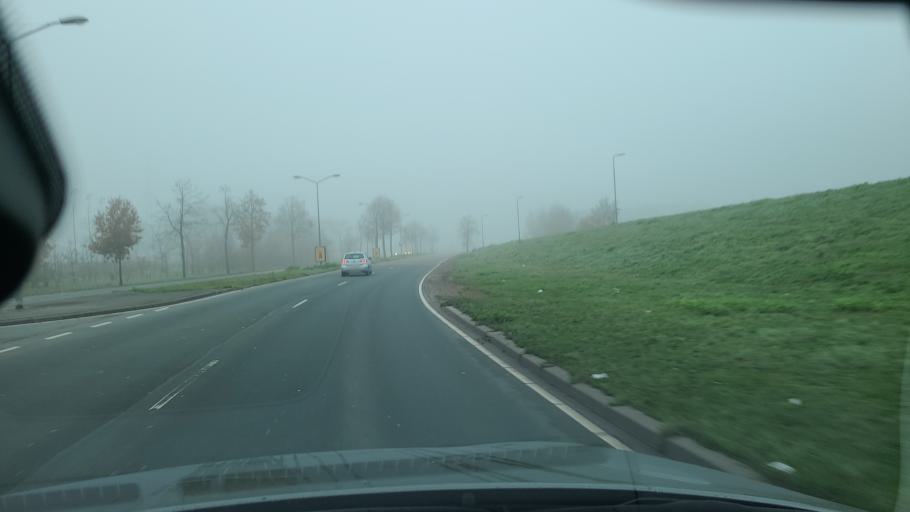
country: NL
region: North Brabant
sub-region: Gemeente 's-Hertogenbosch
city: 's-Hertogenbosch
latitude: 51.7203
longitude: 5.3457
